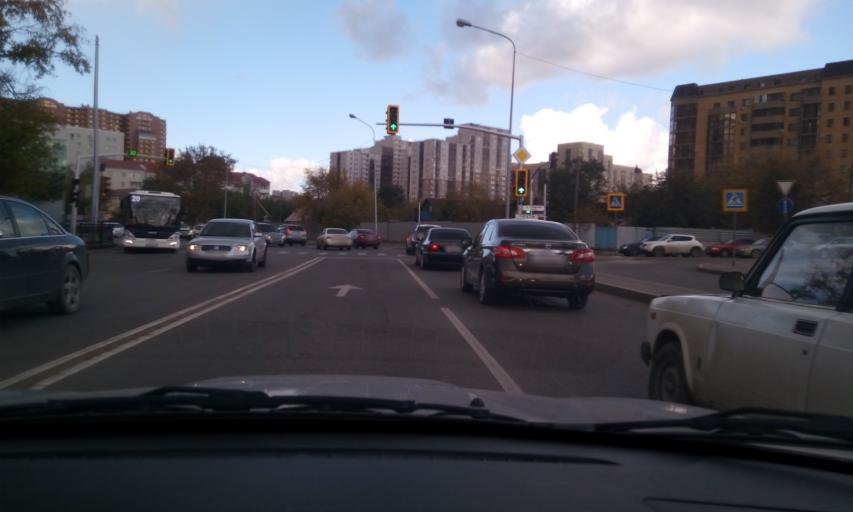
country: KZ
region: Astana Qalasy
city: Astana
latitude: 51.1647
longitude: 71.4471
